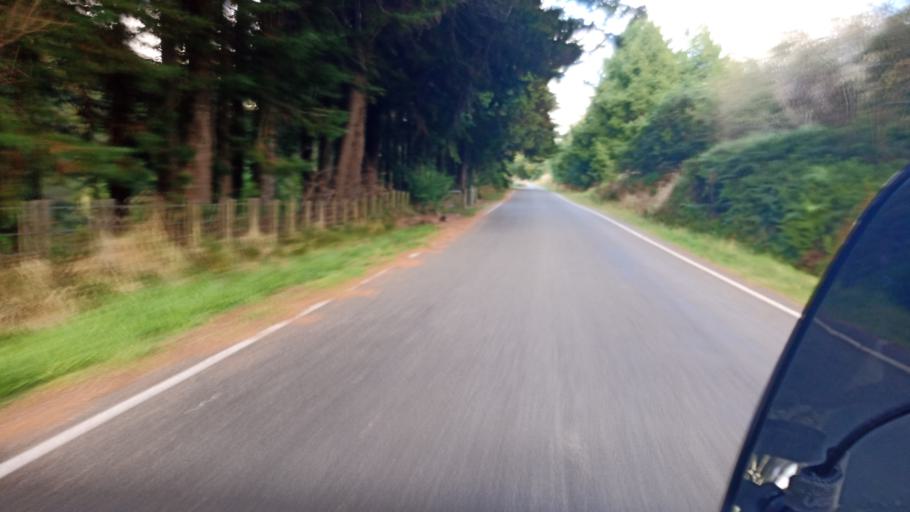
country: NZ
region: Gisborne
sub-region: Gisborne District
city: Gisborne
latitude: -38.5305
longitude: 177.5412
